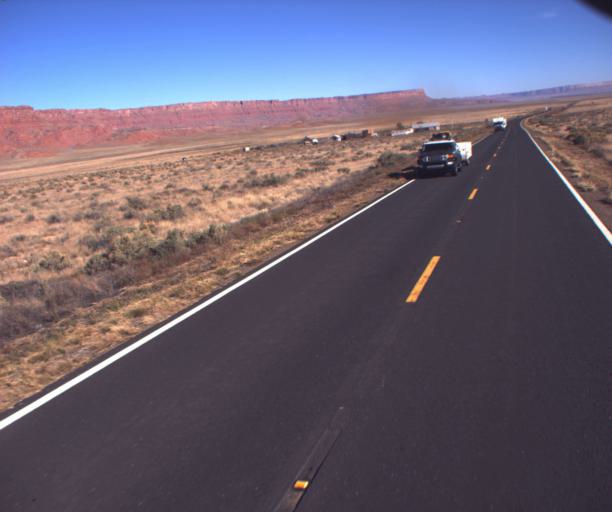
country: US
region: Arizona
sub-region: Coconino County
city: Fredonia
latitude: 36.7321
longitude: -112.0498
